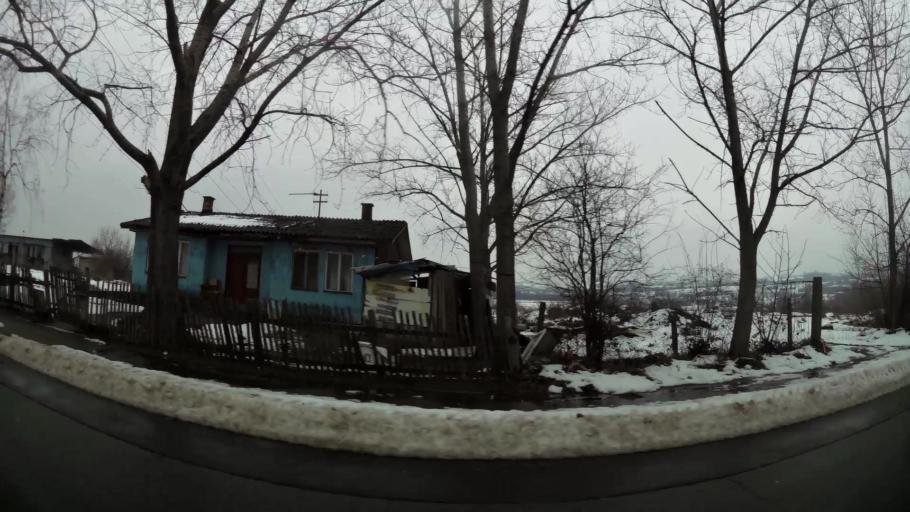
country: RS
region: Central Serbia
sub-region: Belgrade
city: Vozdovac
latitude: 44.7534
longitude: 20.5009
